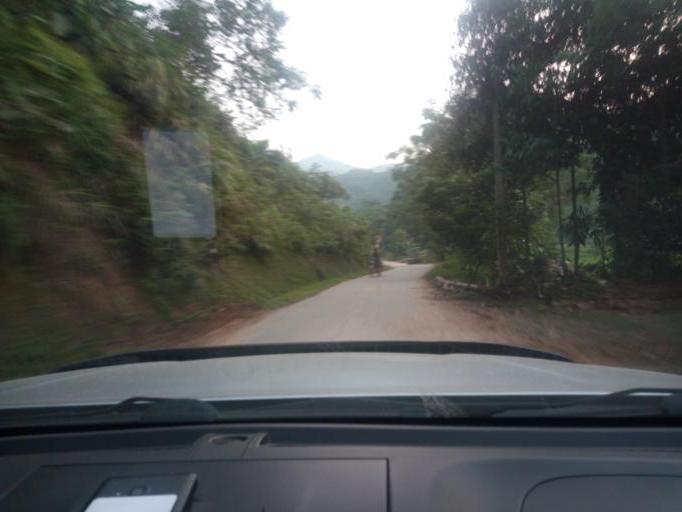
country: VN
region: Yen Bai
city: Co Phuc
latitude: 21.8294
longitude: 104.6258
